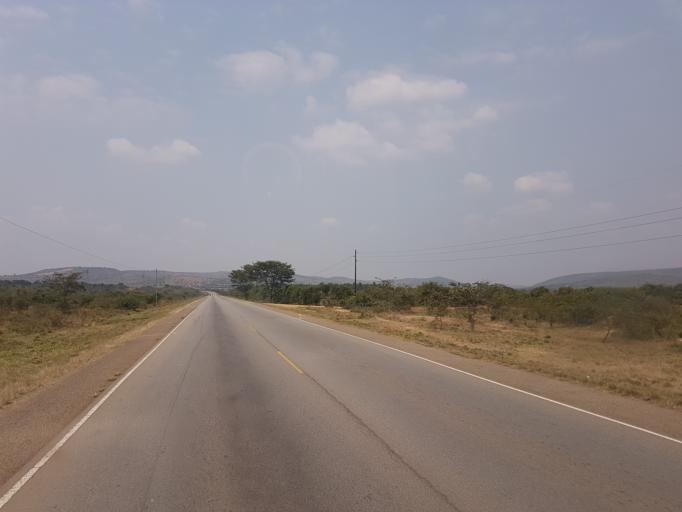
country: UG
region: Western Region
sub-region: Mbarara District
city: Mbarara
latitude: -0.5099
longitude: 30.8303
